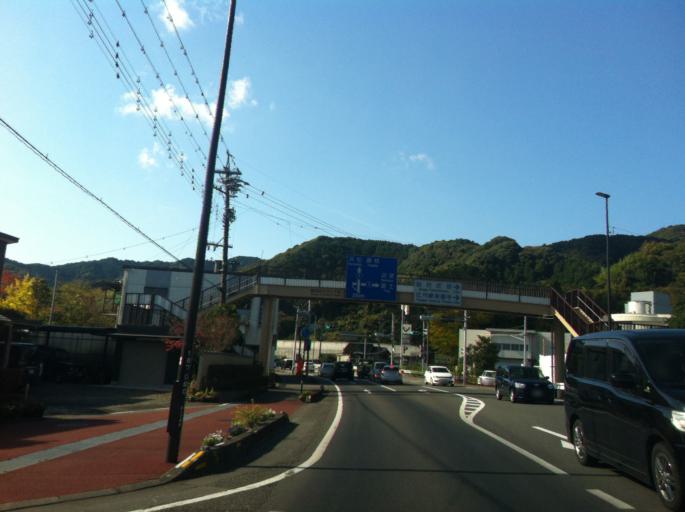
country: JP
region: Shizuoka
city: Shizuoka-shi
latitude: 34.9513
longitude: 138.3356
